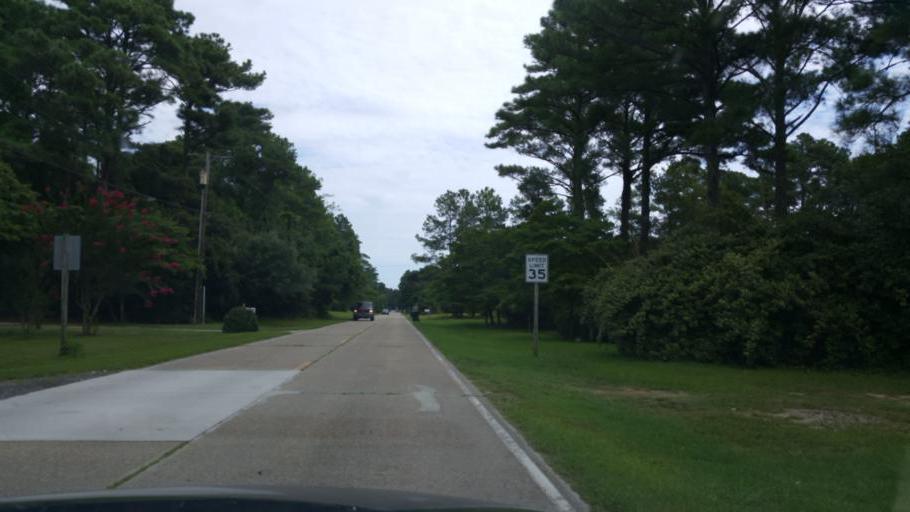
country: US
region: North Carolina
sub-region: Dare County
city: Manteo
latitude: 35.9287
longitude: -75.6971
